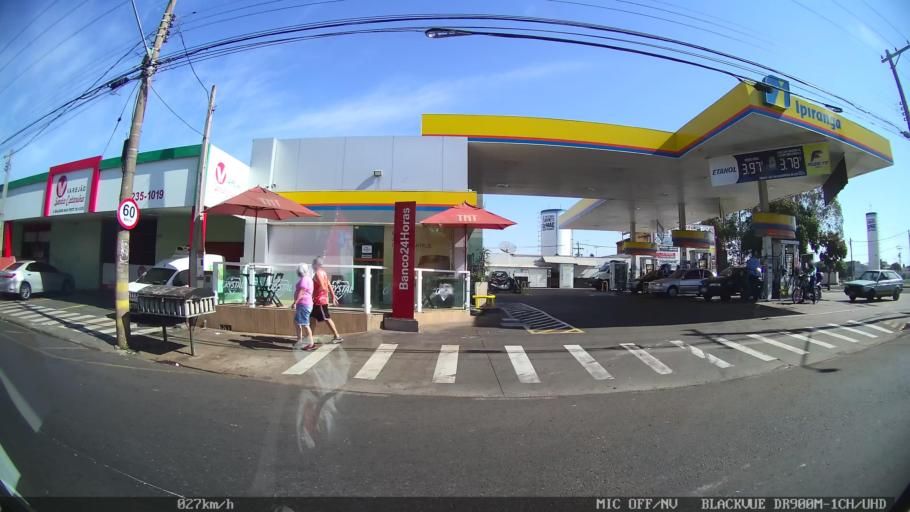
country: BR
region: Sao Paulo
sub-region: Sao Jose Do Rio Preto
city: Sao Jose do Rio Preto
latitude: -20.7772
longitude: -49.3670
